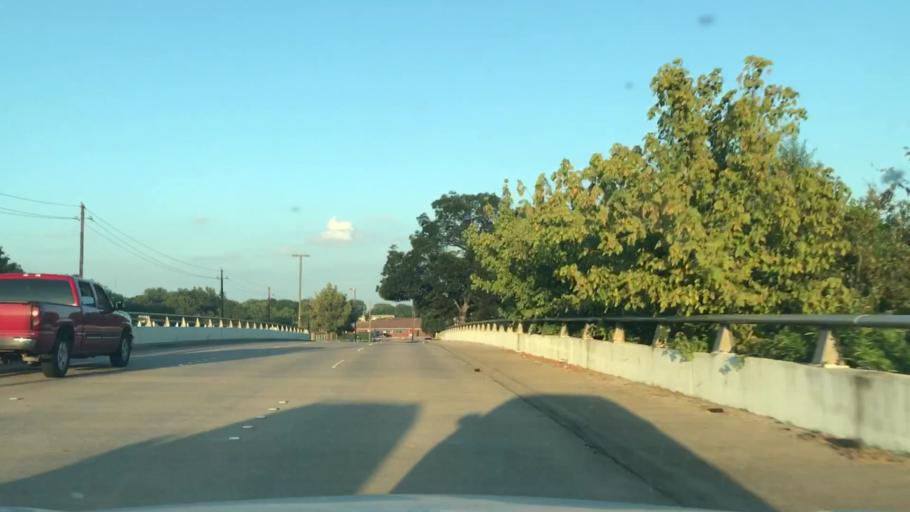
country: US
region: Texas
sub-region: Dallas County
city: Mesquite
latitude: 32.7466
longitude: -96.6023
